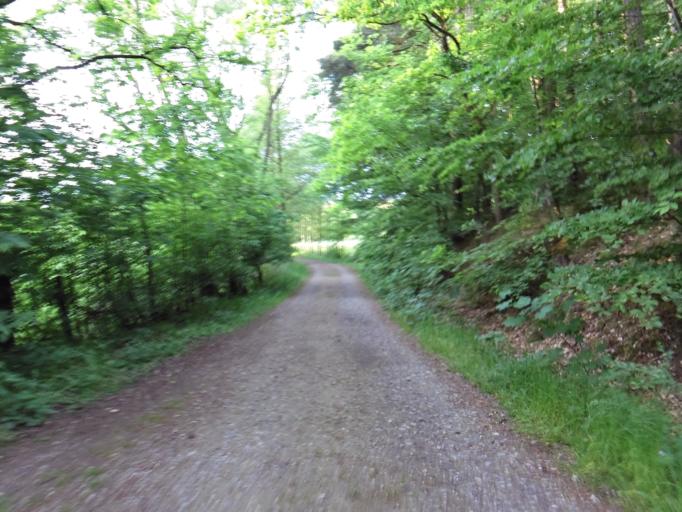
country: DE
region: Thuringia
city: Frauensee
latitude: 50.9051
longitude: 10.1082
